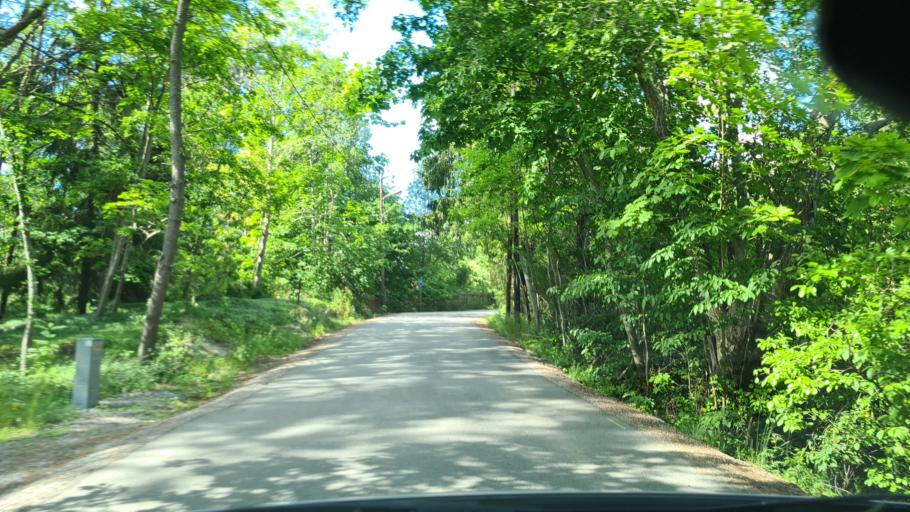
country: SE
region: Stockholm
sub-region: Vaxholms Kommun
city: Vaxholm
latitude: 59.4106
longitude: 18.3720
